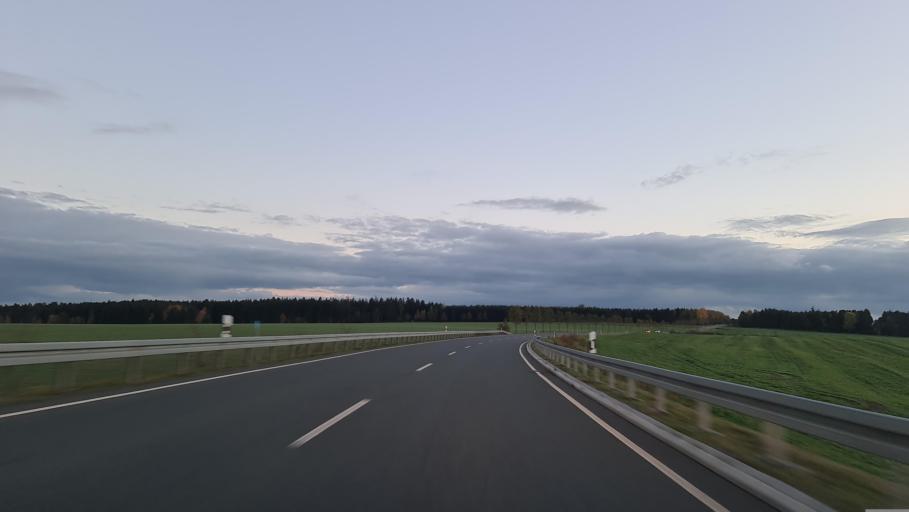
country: DE
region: Thuringia
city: Dittersdorf
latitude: 50.6381
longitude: 11.8148
